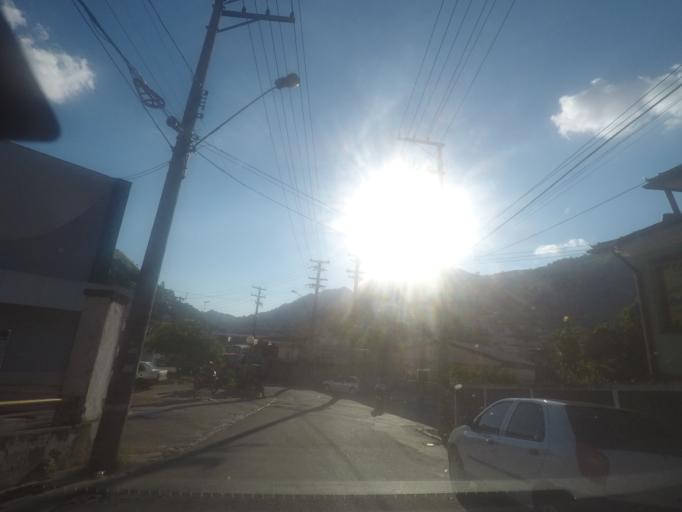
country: BR
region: Rio de Janeiro
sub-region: Petropolis
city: Petropolis
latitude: -22.4865
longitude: -43.1509
